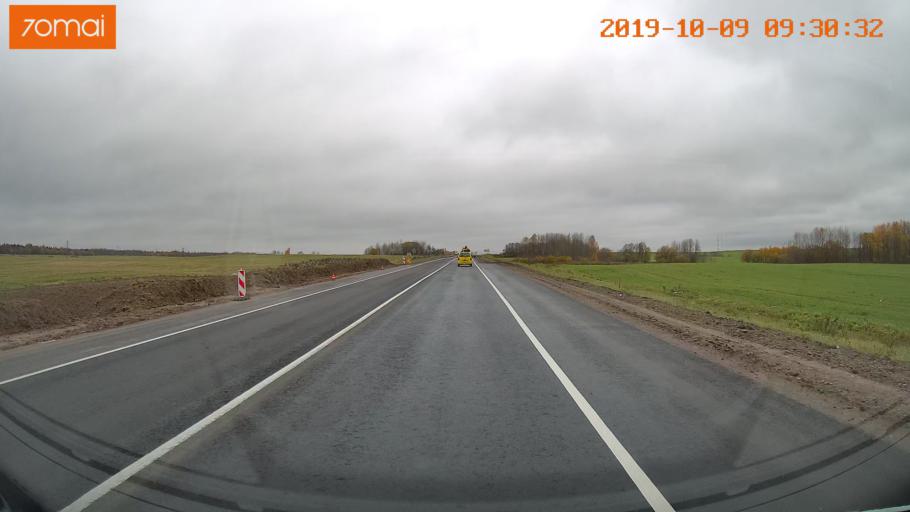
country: RU
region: Vologda
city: Vologda
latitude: 59.1407
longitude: 39.9481
